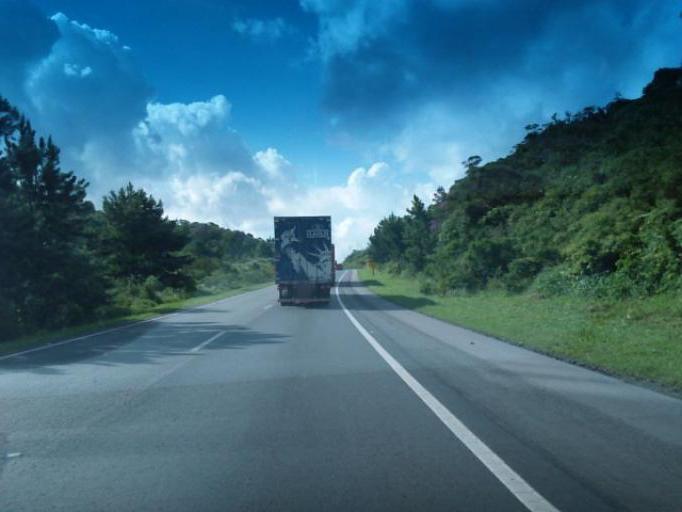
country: BR
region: Parana
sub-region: Campina Grande Do Sul
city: Campina Grande do Sul
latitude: -25.1026
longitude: -48.8094
